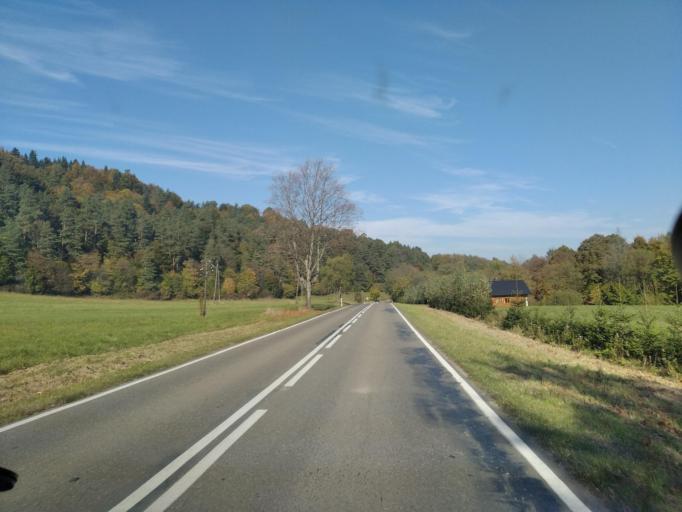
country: PL
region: Subcarpathian Voivodeship
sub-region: Powiat leski
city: Lesko
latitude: 49.4115
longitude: 22.3035
